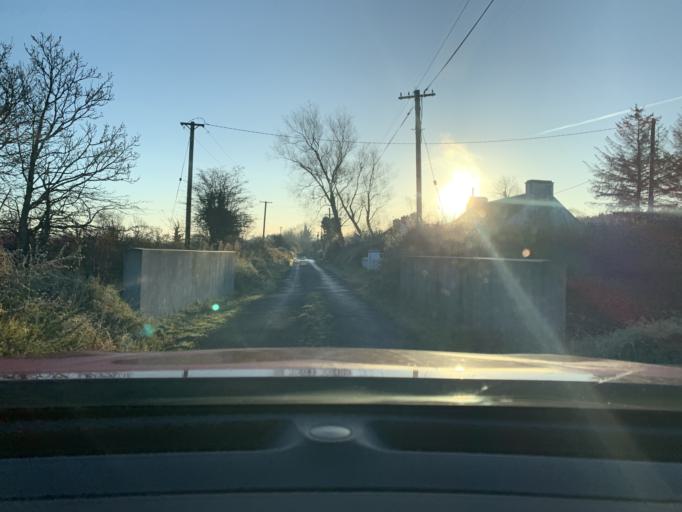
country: IE
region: Connaught
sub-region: Sligo
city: Ballymote
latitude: 53.9869
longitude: -8.5257
